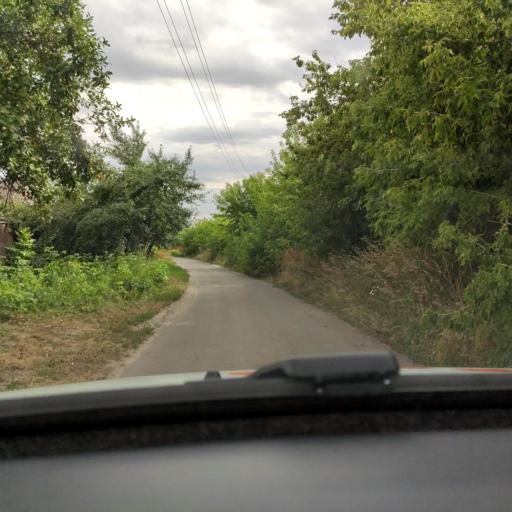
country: RU
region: Voronezj
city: Orlovo
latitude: 51.6504
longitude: 39.5705
